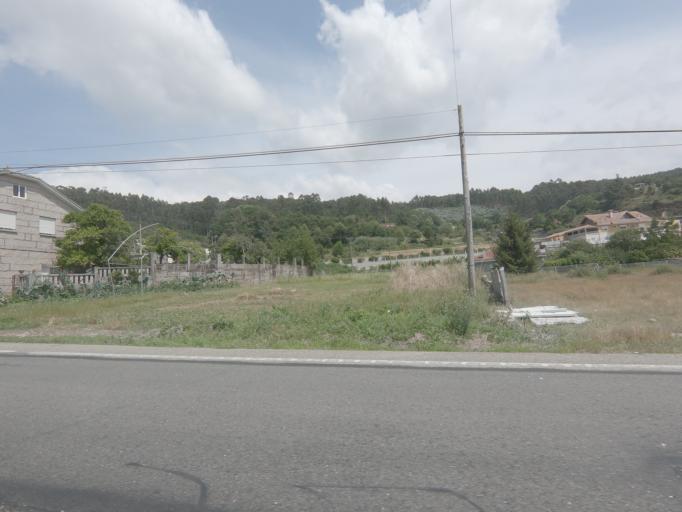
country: ES
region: Galicia
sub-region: Provincia de Pontevedra
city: Tomino
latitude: 42.0369
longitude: -8.7283
